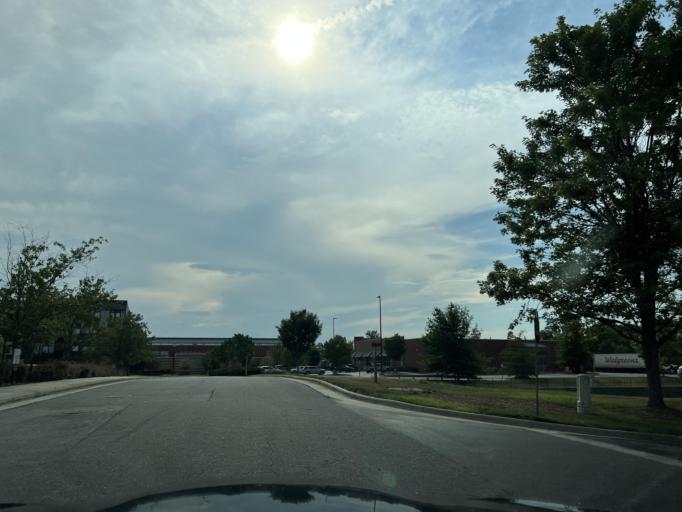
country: US
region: North Carolina
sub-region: Wake County
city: Morrisville
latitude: 35.9016
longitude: -78.8023
